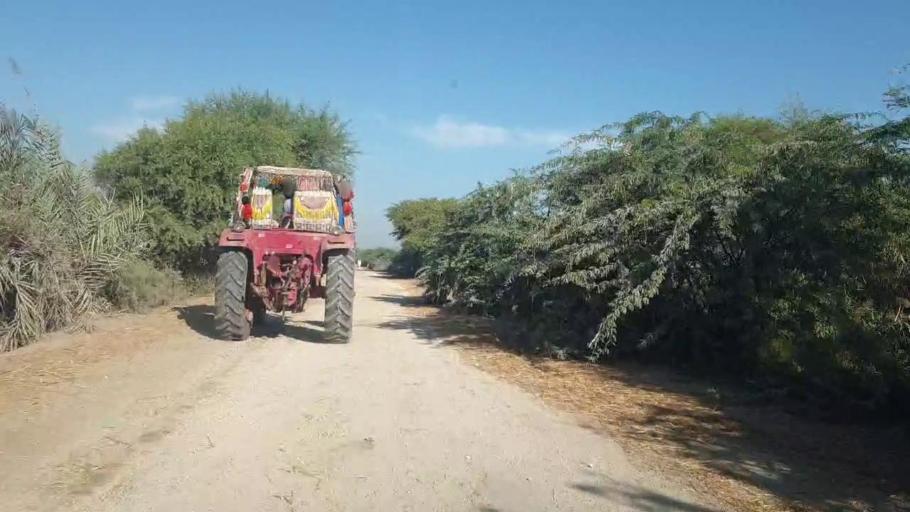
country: PK
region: Sindh
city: Talhar
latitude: 24.9061
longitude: 68.8103
